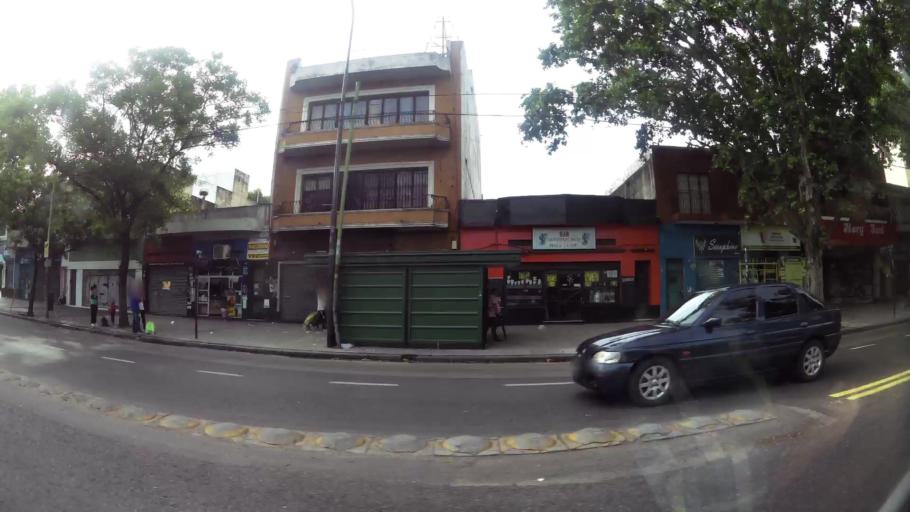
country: AR
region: Buenos Aires F.D.
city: Villa Lugano
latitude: -34.6457
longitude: -58.4668
